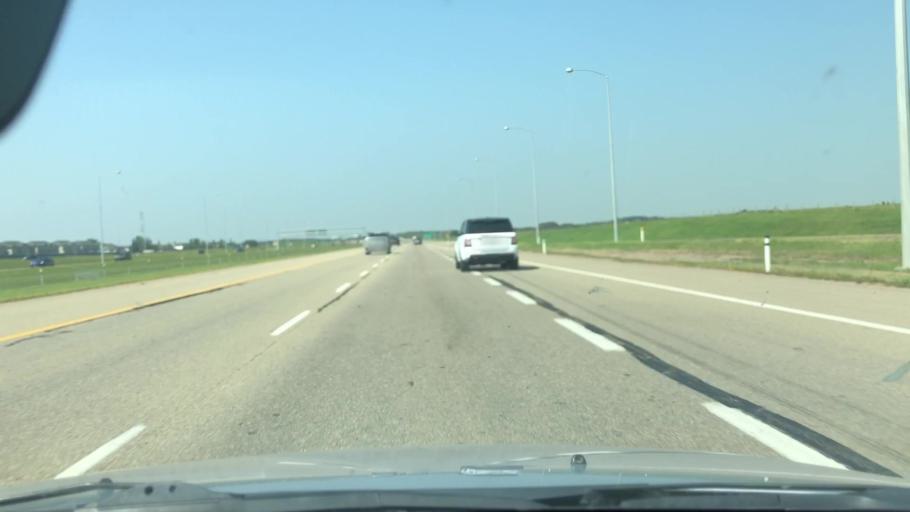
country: CA
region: Alberta
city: Edmonton
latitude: 53.6472
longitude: -113.4954
